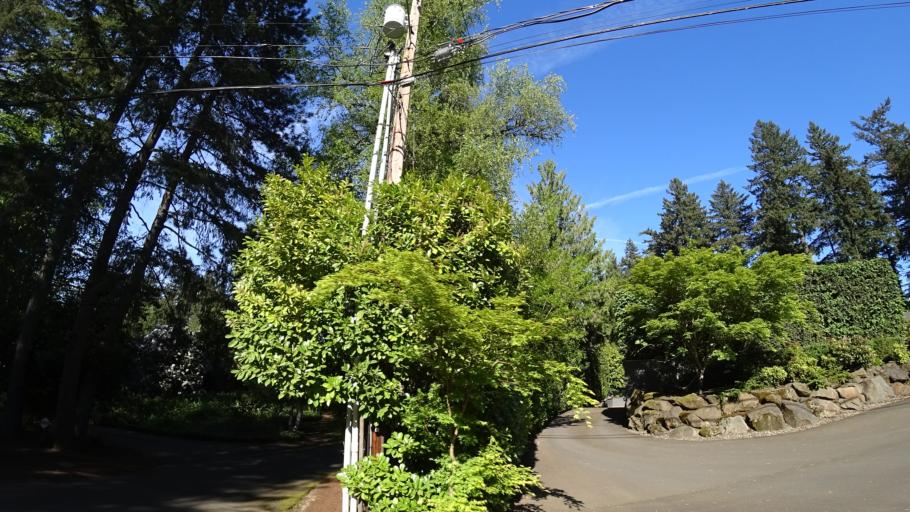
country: US
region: Oregon
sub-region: Washington County
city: Raleigh Hills
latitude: 45.4888
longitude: -122.7525
